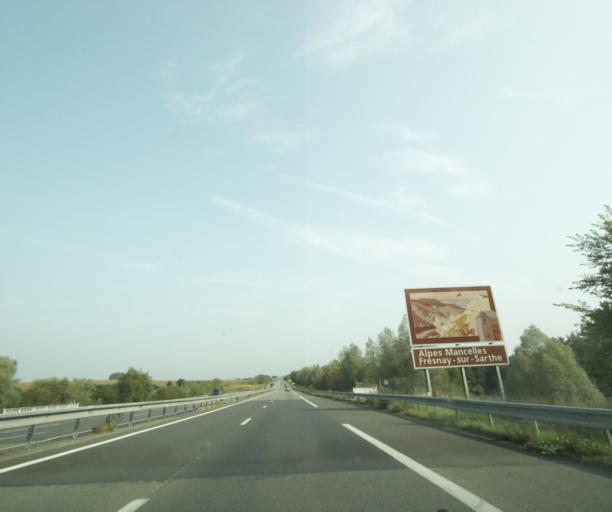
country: FR
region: Pays de la Loire
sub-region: Departement de la Sarthe
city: Sainte-Jamme-sur-Sarthe
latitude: 48.1506
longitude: 0.1434
